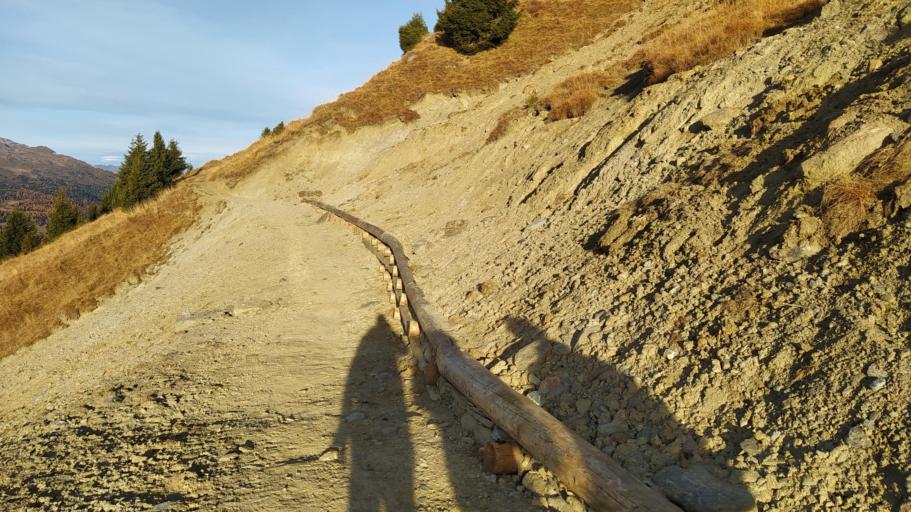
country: IT
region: Lombardy
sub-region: Provincia di Sondrio
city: Sant'Antonio
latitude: 46.4242
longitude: 10.4963
